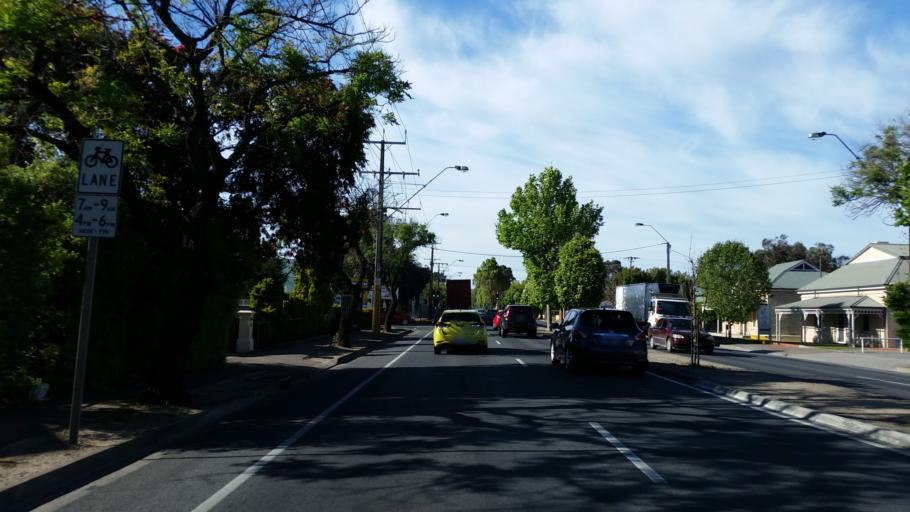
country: AU
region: South Australia
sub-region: Norwood Payneham St Peters
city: Royston Park
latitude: -34.9012
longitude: 138.6396
